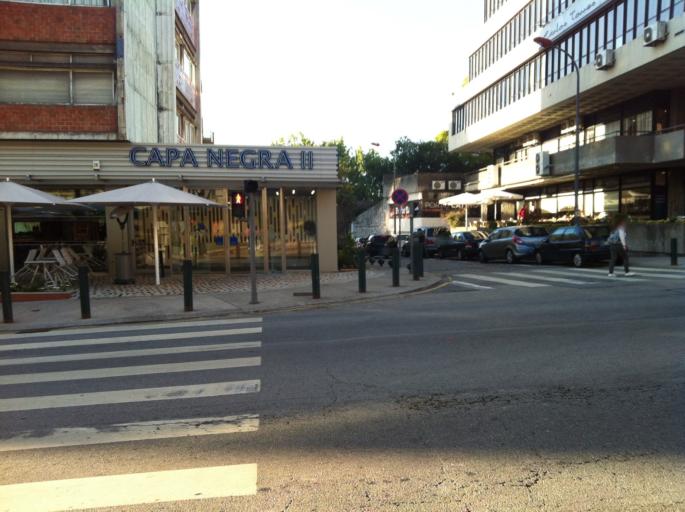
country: PT
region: Porto
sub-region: Porto
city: Porto
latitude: 41.1527
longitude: -8.6305
